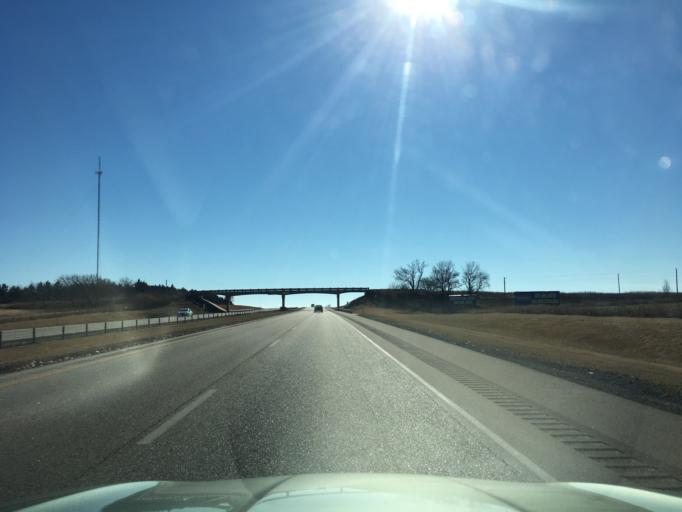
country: US
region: Oklahoma
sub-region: Kay County
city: Blackwell
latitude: 36.8712
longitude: -97.3493
